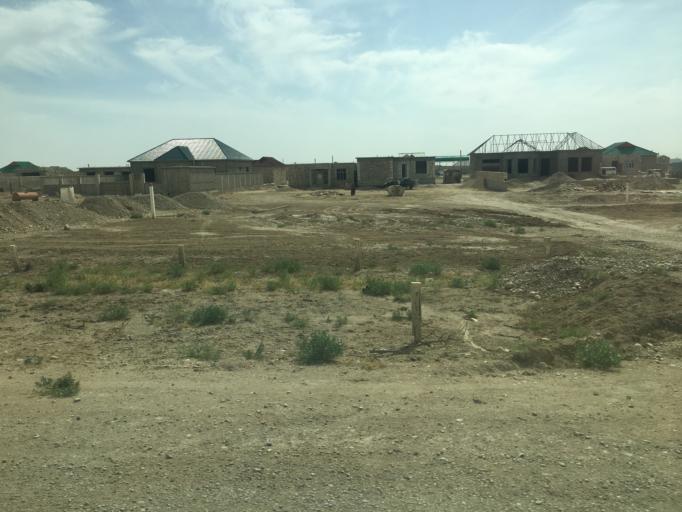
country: TM
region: Balkan
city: Balkanabat
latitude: 39.6155
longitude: 54.2496
